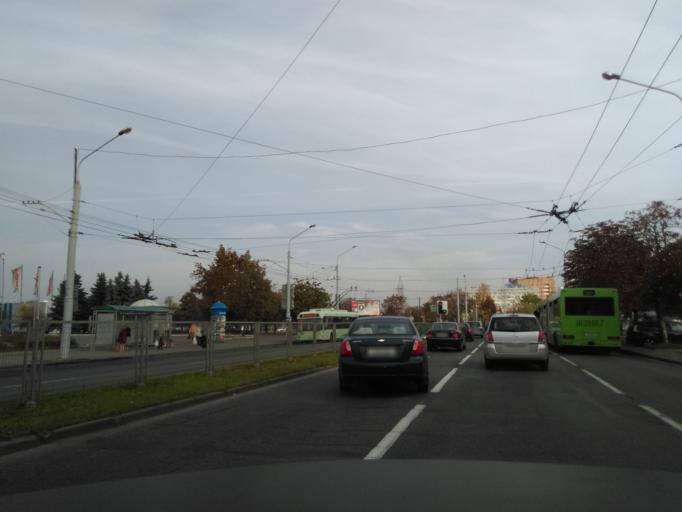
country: BY
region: Minsk
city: Minsk
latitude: 53.8750
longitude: 27.5970
